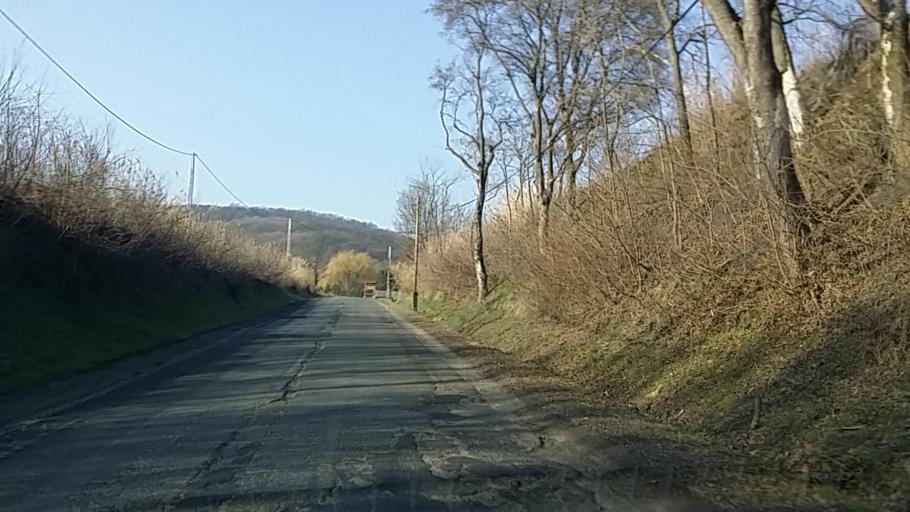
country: HU
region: Komarom-Esztergom
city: Tat
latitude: 47.7311
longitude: 18.6153
